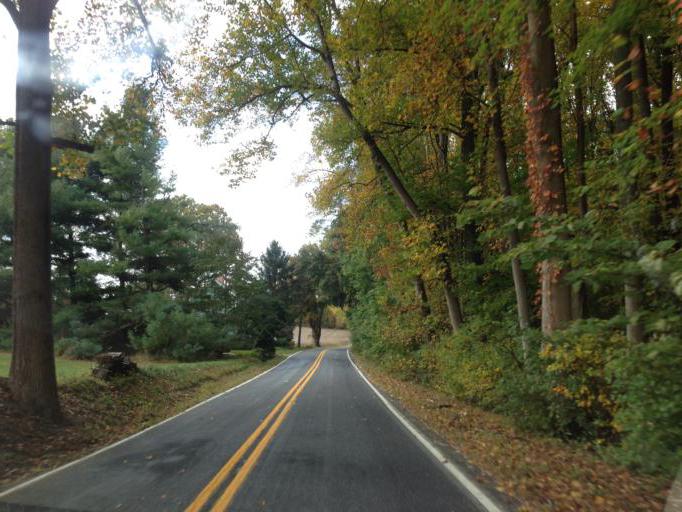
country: US
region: Maryland
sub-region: Carroll County
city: Mount Airy
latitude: 39.3182
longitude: -77.1296
